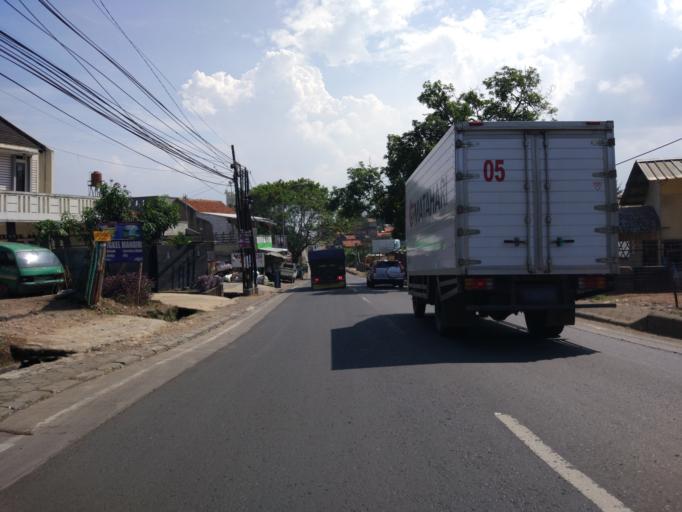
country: ID
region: West Java
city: Cileunyi
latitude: -6.9404
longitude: 107.7471
